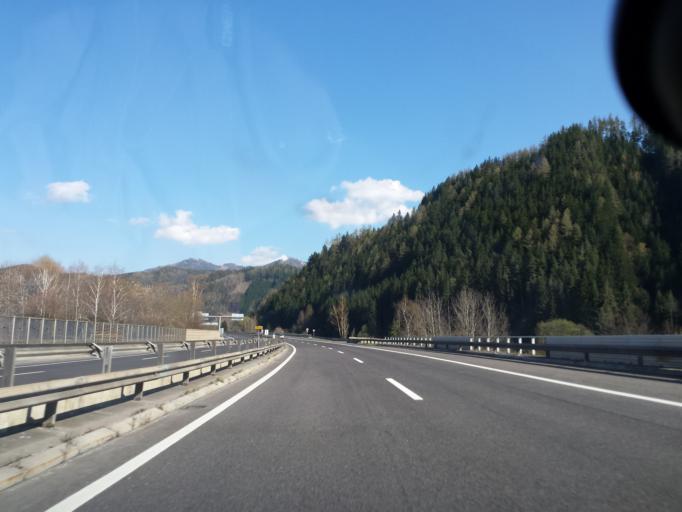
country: AT
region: Styria
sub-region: Politischer Bezirk Leoben
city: Sankt Michael in Obersteiermark
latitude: 47.3356
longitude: 15.0118
